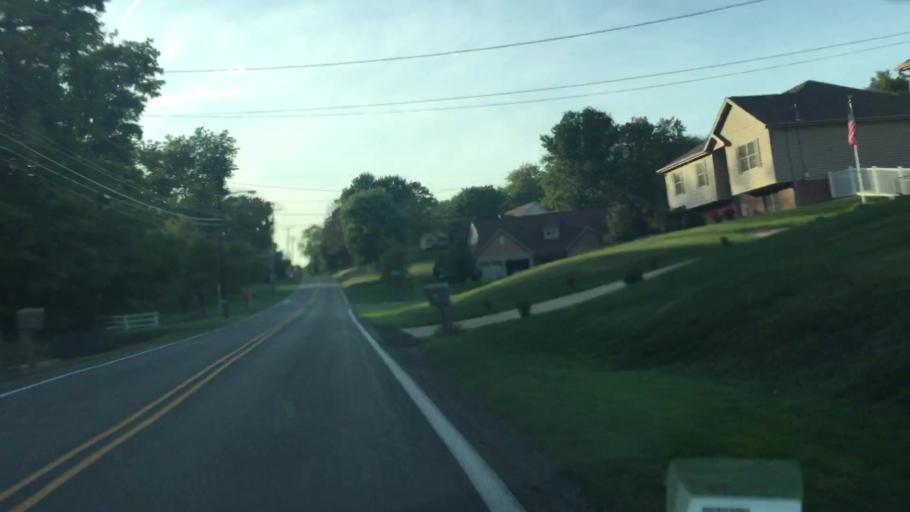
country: US
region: Pennsylvania
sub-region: Beaver County
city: Ambridge
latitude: 40.5700
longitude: -80.2672
